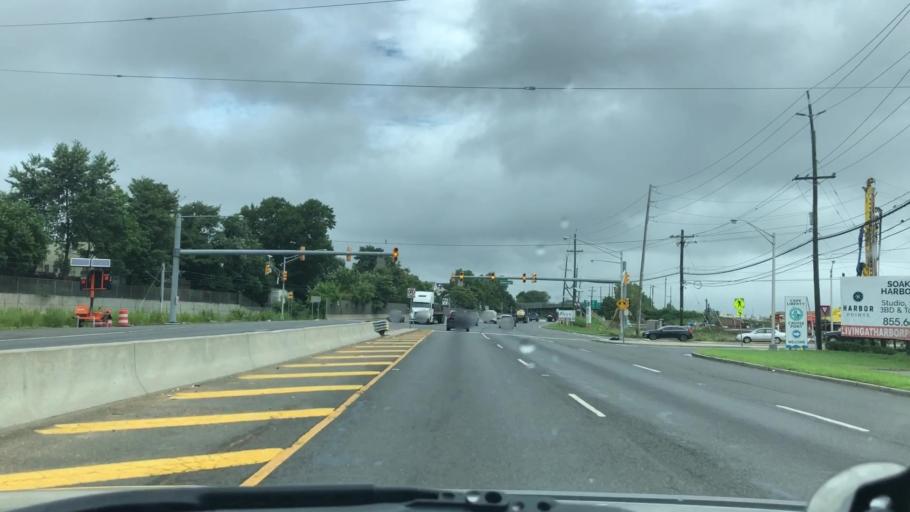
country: US
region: New Jersey
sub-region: Hudson County
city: Bayonne
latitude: 40.6719
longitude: -74.1066
